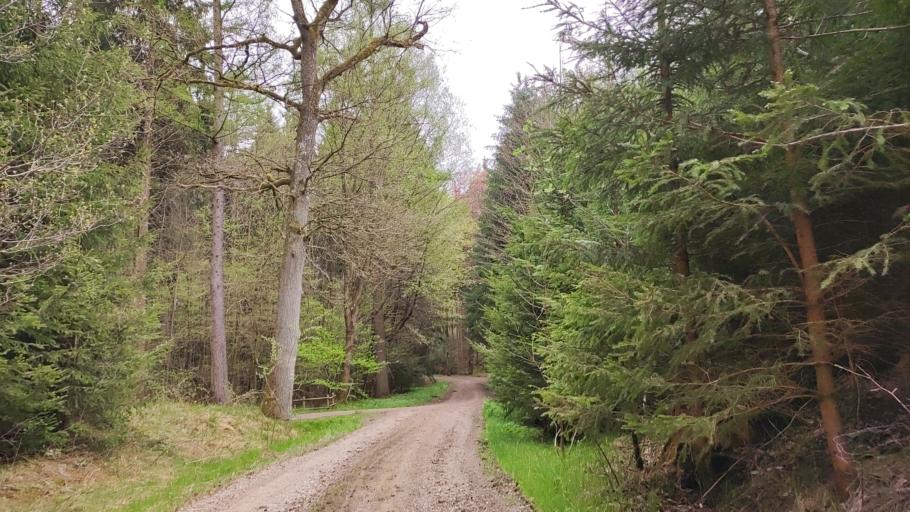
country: DE
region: Bavaria
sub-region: Swabia
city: Holzheim
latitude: 48.4842
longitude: 10.5470
